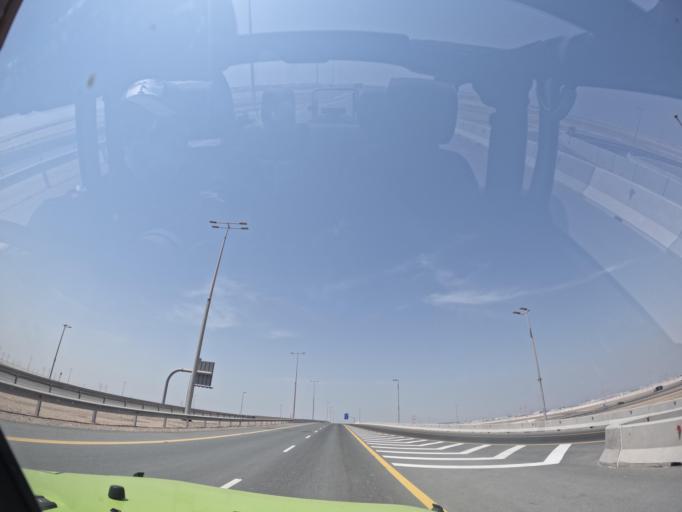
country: AE
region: Abu Dhabi
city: Abu Dhabi
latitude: 24.2454
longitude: 54.4749
